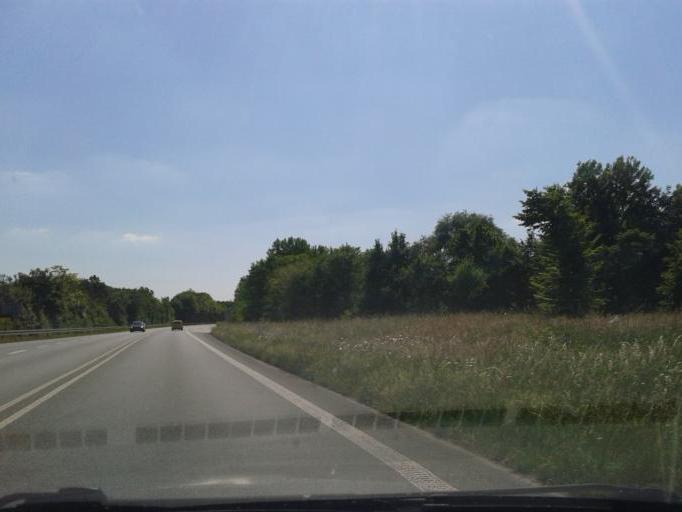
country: DE
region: North Rhine-Westphalia
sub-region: Regierungsbezirk Detmold
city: Paderborn
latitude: 51.7409
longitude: 8.7323
